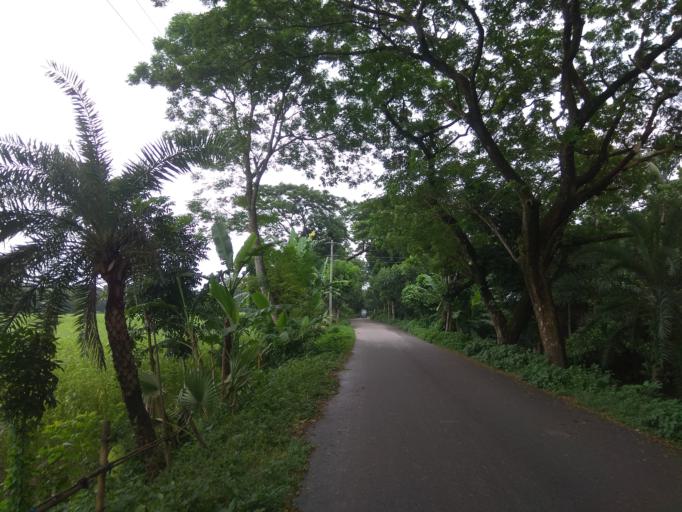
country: BD
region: Dhaka
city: Dohar
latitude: 23.4199
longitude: 90.0679
